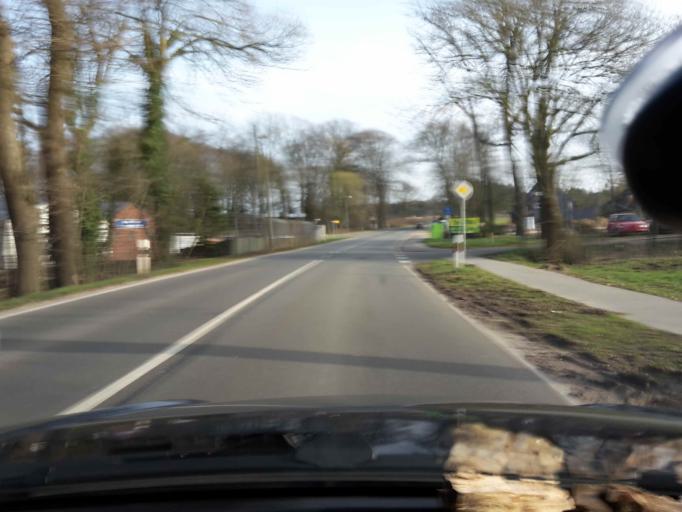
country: DE
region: Lower Saxony
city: Buchholz in der Nordheide
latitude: 53.3511
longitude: 9.8807
